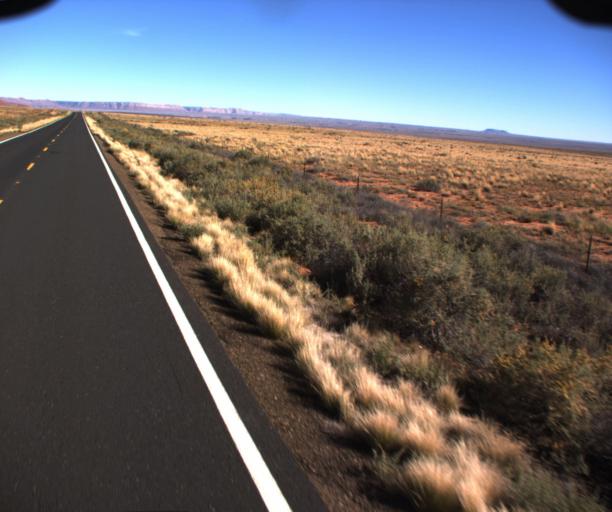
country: US
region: Arizona
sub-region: Coconino County
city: Page
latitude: 36.7097
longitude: -111.9675
